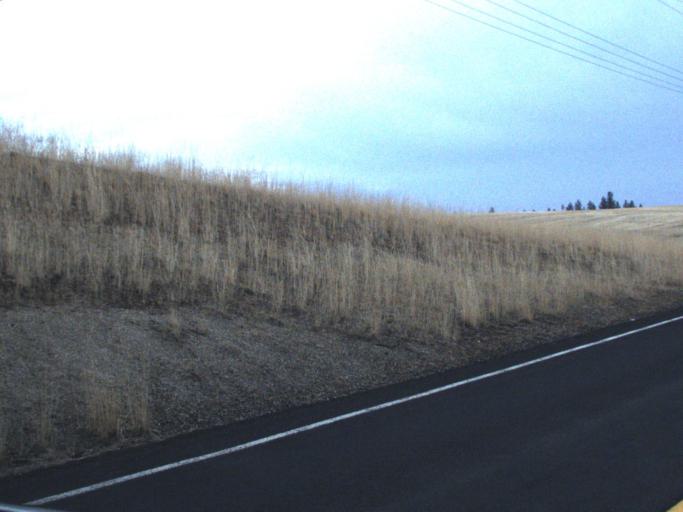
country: US
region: Washington
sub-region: Lincoln County
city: Davenport
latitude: 47.8276
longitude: -118.2054
